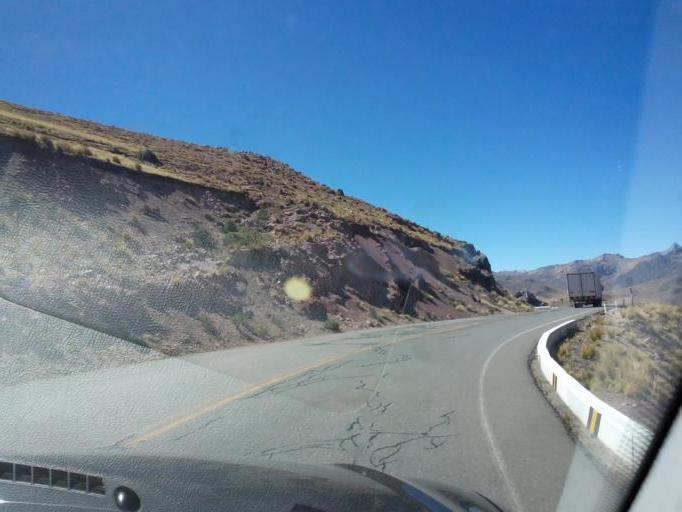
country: PE
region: Huancavelica
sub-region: Huaytara
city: Pilpichaca
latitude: -13.4099
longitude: -74.9540
